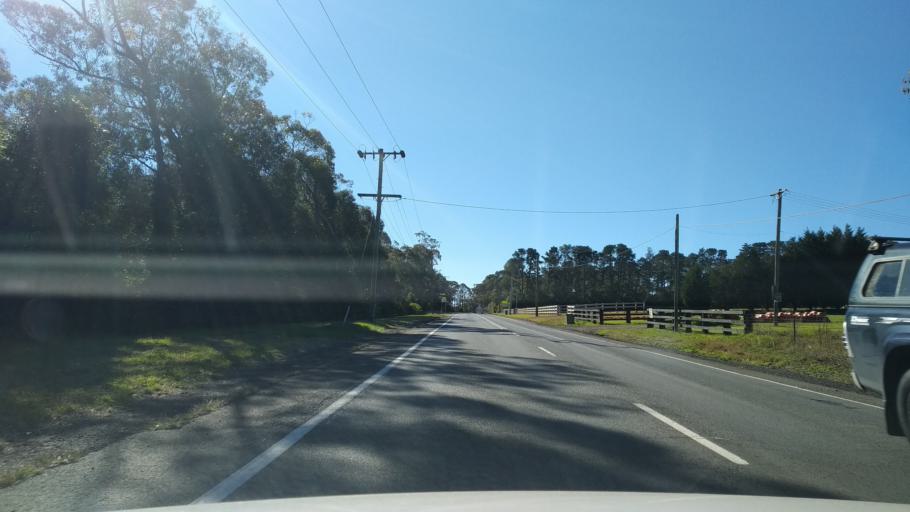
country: AU
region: New South Wales
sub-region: Gosford Shire
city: Narara
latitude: -33.3292
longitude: 151.2312
